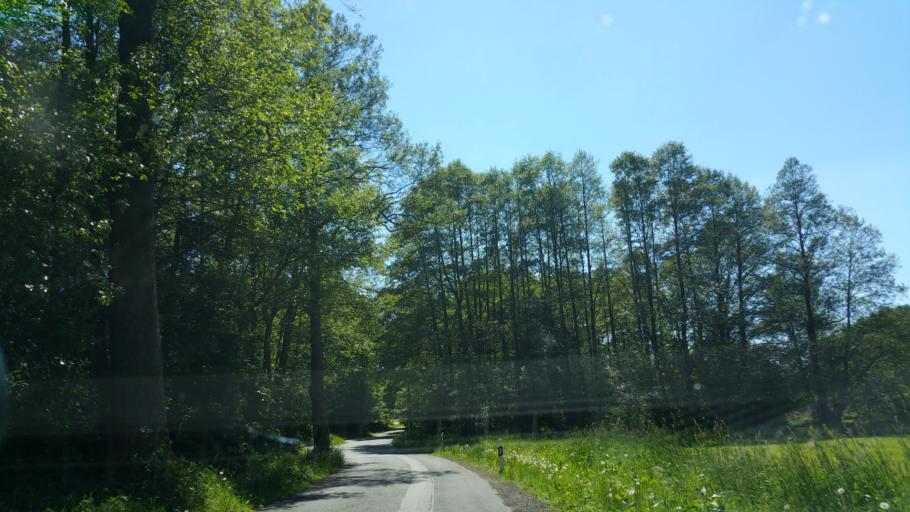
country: DE
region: Bavaria
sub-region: Upper Franconia
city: Schwarzenbach an der Saale
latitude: 50.2183
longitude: 11.9333
